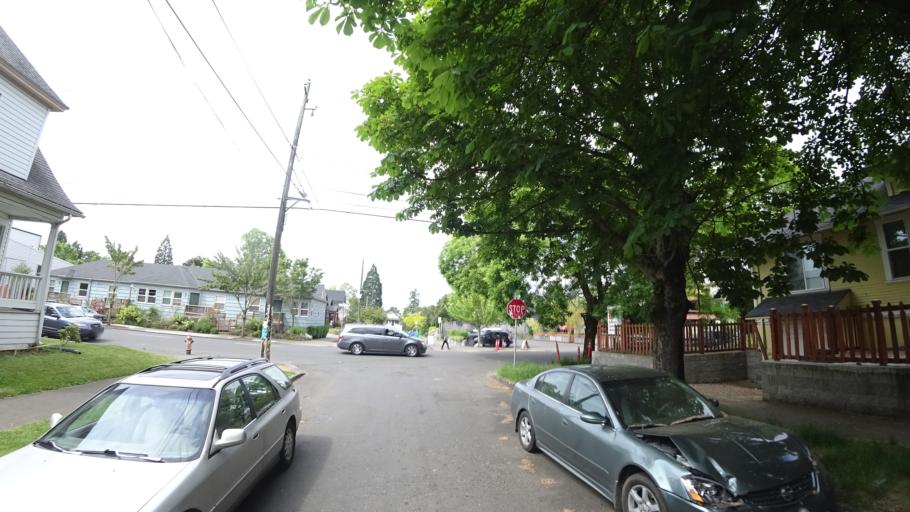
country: US
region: Oregon
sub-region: Multnomah County
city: Portland
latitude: 45.5589
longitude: -122.6556
